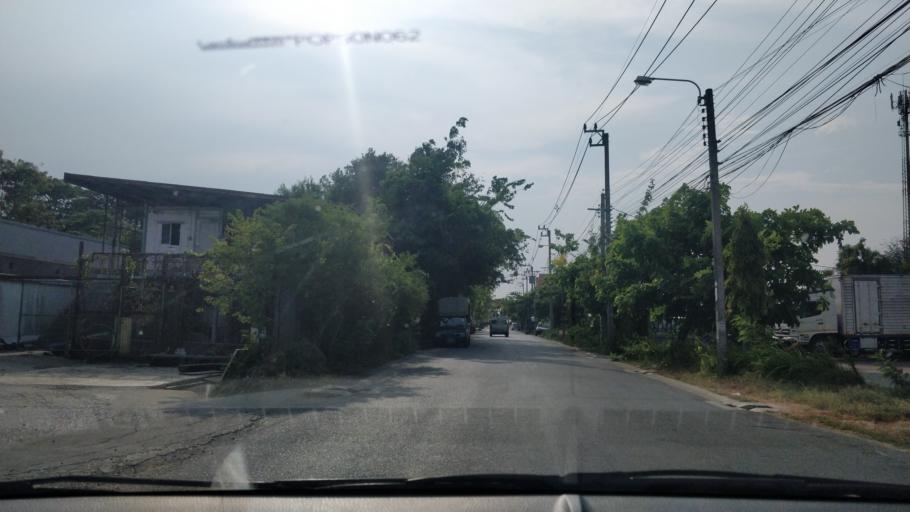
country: TH
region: Bangkok
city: Saphan Sung
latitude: 13.7341
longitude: 100.6982
